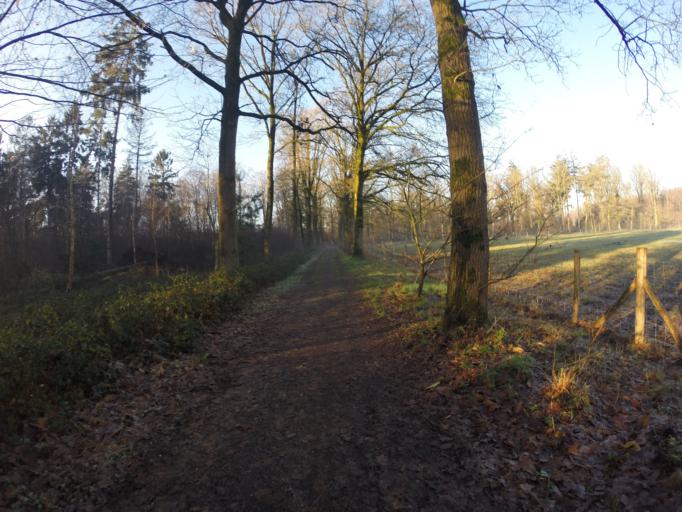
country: BE
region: Flanders
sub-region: Provincie West-Vlaanderen
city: Beernem
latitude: 51.0959
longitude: 3.3264
